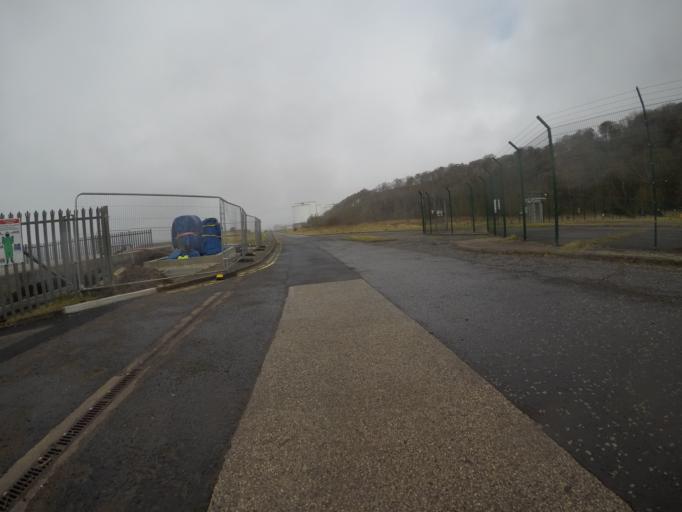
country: GB
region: Scotland
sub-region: North Ayrshire
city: Millport
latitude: 55.7148
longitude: -4.9030
